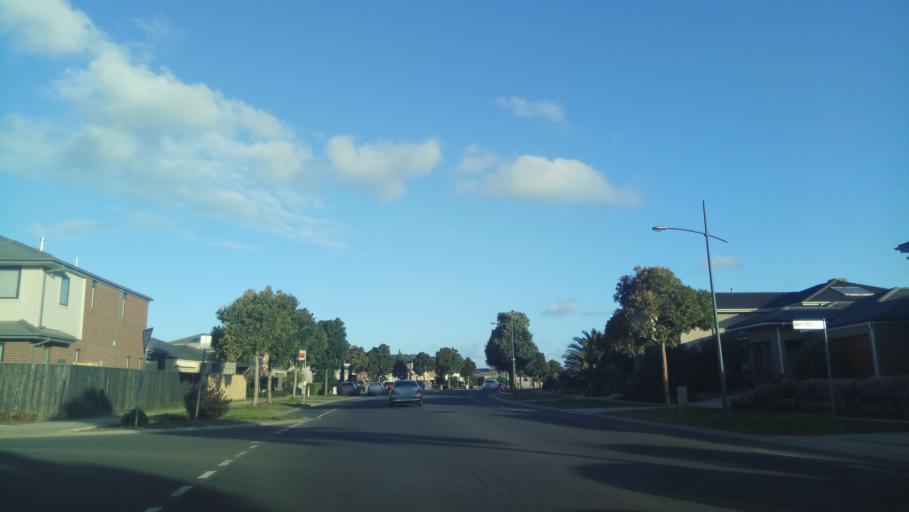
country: AU
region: Victoria
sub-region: Wyndham
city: Point Cook
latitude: -37.9096
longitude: 144.7751
